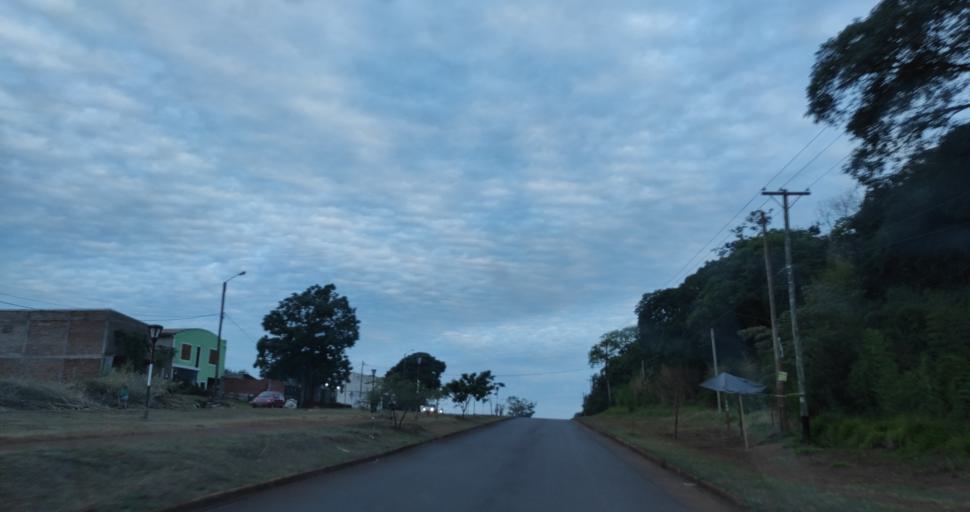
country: AR
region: Misiones
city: Garupa
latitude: -27.4672
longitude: -55.8528
